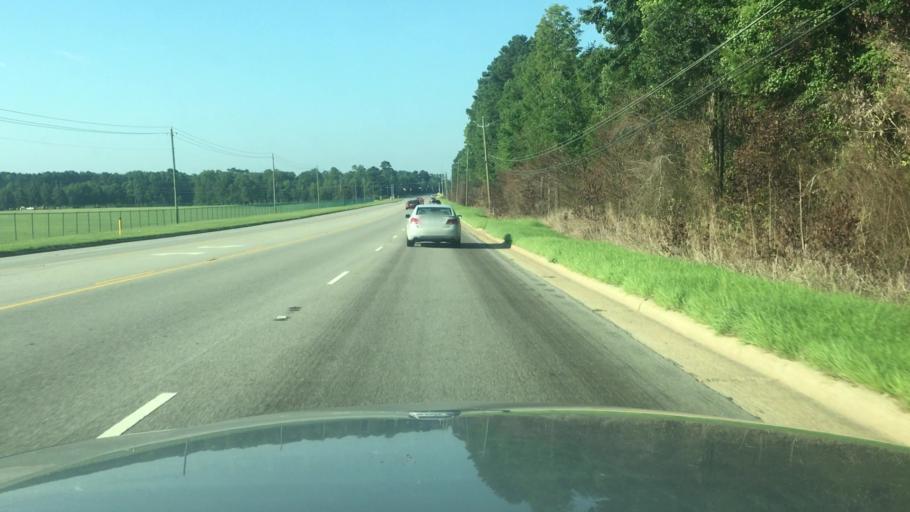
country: US
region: North Carolina
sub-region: Cumberland County
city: Eastover
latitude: 35.1727
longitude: -78.8609
